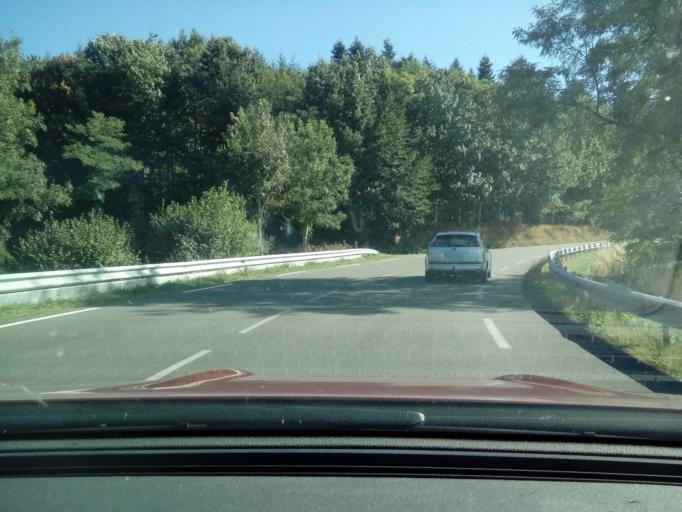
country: FR
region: Rhone-Alpes
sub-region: Departement du Rhone
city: Cublize
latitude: 45.9788
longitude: 4.3940
